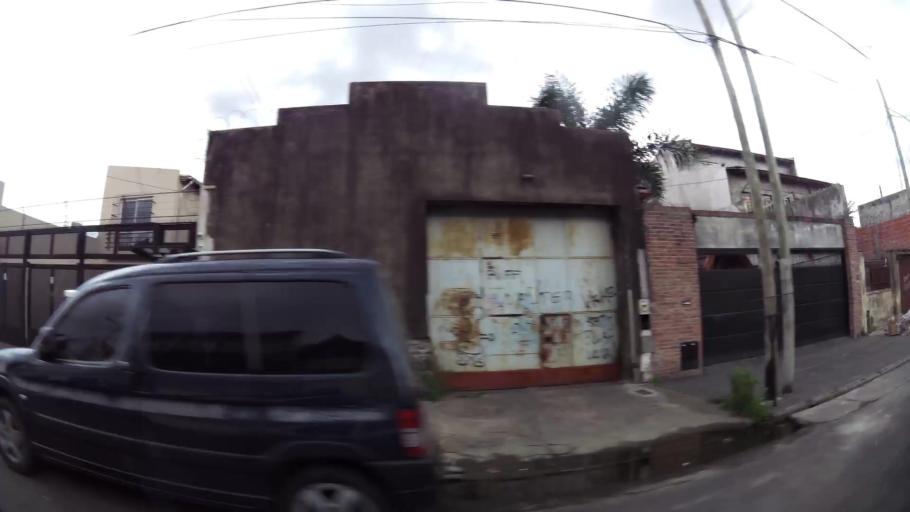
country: AR
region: Buenos Aires
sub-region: Partido de Avellaneda
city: Avellaneda
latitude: -34.6782
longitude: -58.3861
